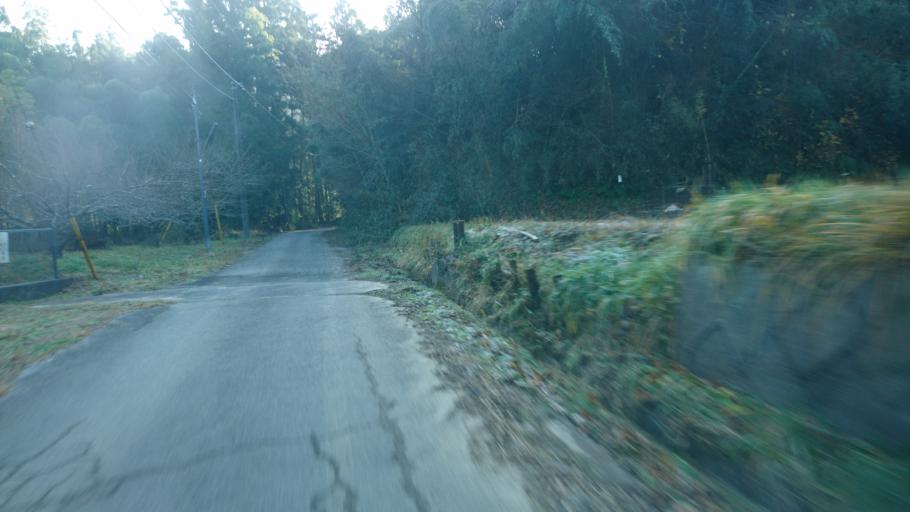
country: JP
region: Chiba
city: Kimitsu
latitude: 35.2900
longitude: 139.9538
